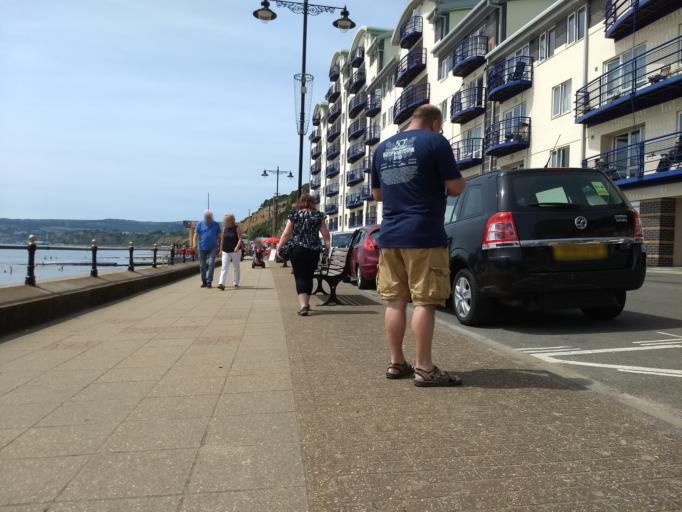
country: GB
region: England
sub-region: Isle of Wight
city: Sandown
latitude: 50.6521
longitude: -1.1567
